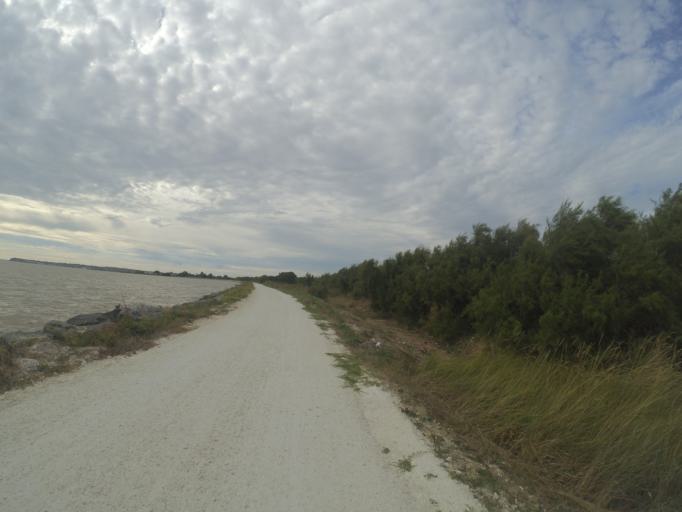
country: FR
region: Poitou-Charentes
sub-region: Departement de la Charente-Maritime
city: Meschers-sur-Gironde
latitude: 45.5476
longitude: -0.9132
